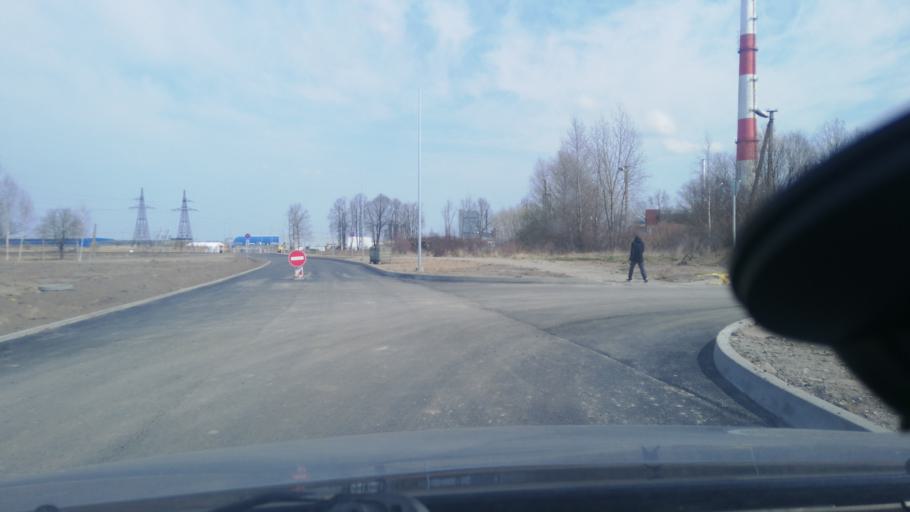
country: LT
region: Klaipedos apskritis
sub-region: Klaipeda
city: Klaipeda
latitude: 55.6818
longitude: 21.1960
